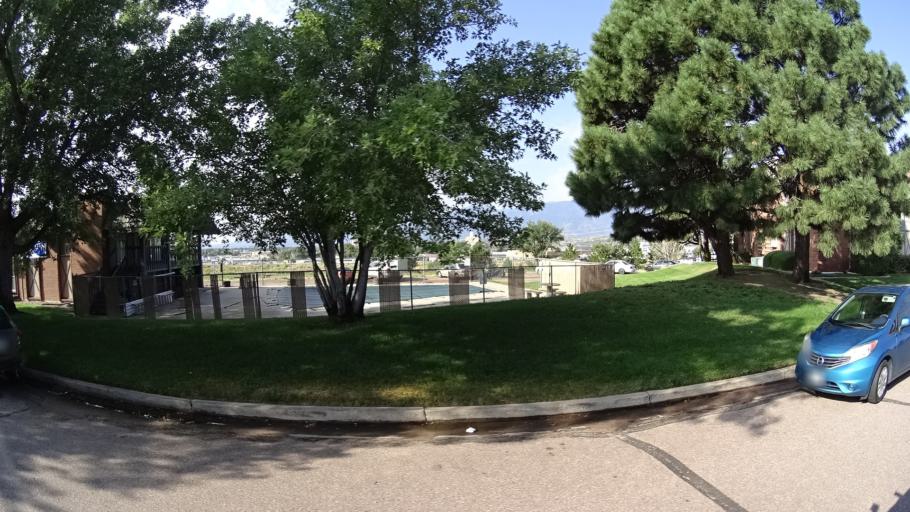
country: US
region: Colorado
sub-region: El Paso County
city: Colorado Springs
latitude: 38.8879
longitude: -104.8107
